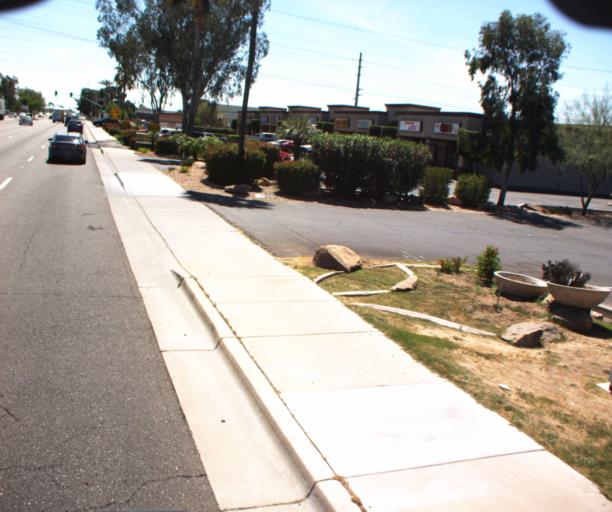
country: US
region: Arizona
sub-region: Maricopa County
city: San Carlos
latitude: 33.3582
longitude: -111.8419
